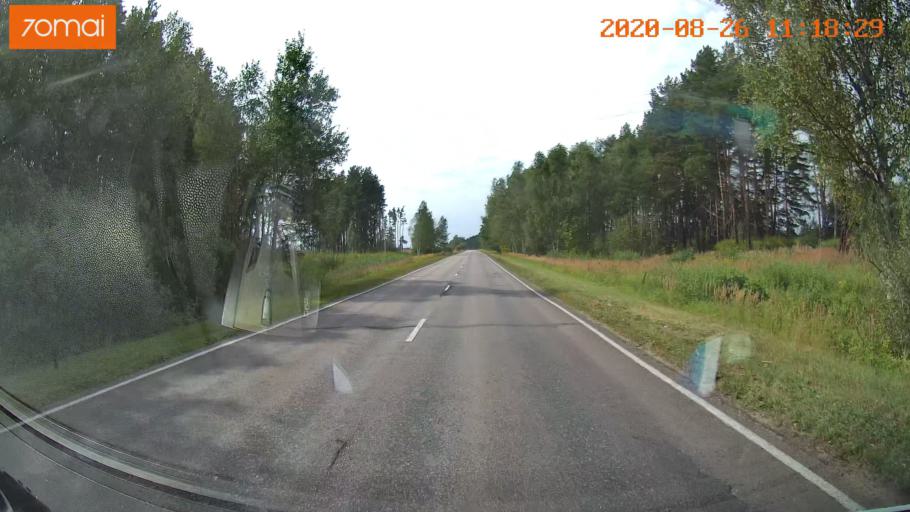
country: RU
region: Rjazan
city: Shilovo
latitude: 54.4097
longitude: 41.0967
